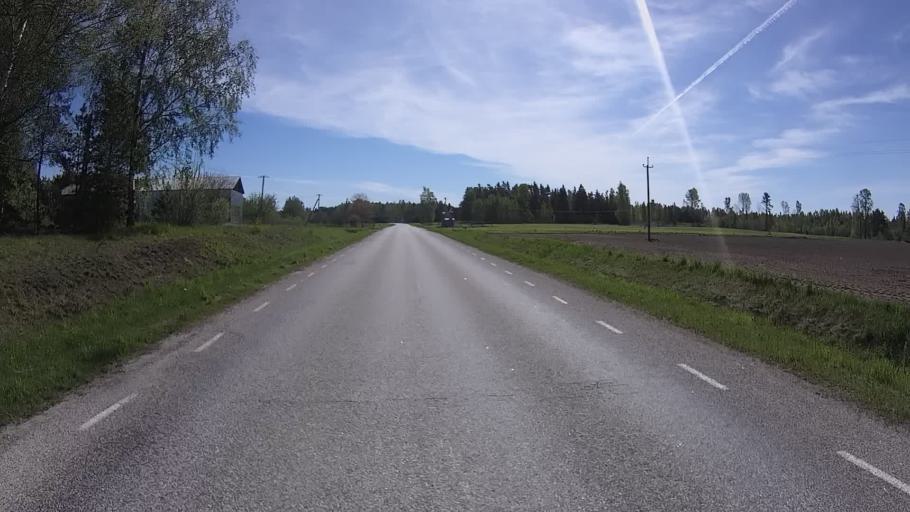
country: EE
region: Polvamaa
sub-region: Raepina vald
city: Rapina
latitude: 57.9676
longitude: 27.5285
